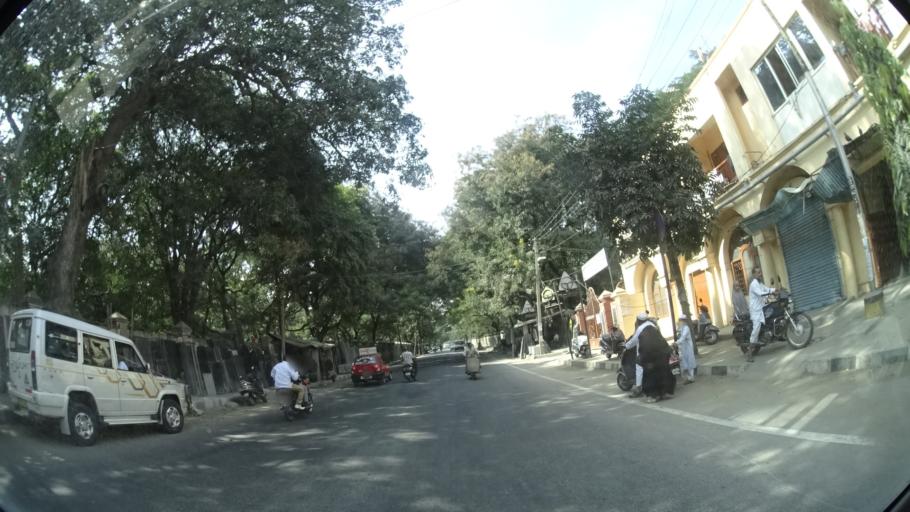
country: IN
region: Karnataka
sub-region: Bangalore Urban
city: Bangalore
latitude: 13.0037
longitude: 77.5958
